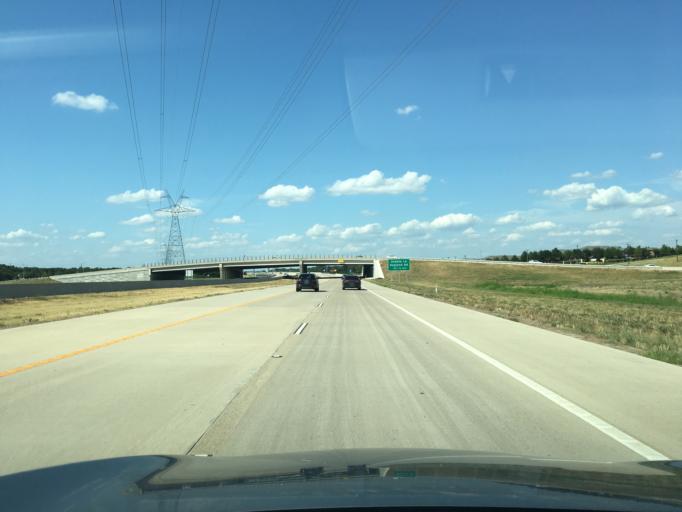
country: US
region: Texas
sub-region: Tarrant County
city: Mansfield
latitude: 32.5804
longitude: -97.0793
